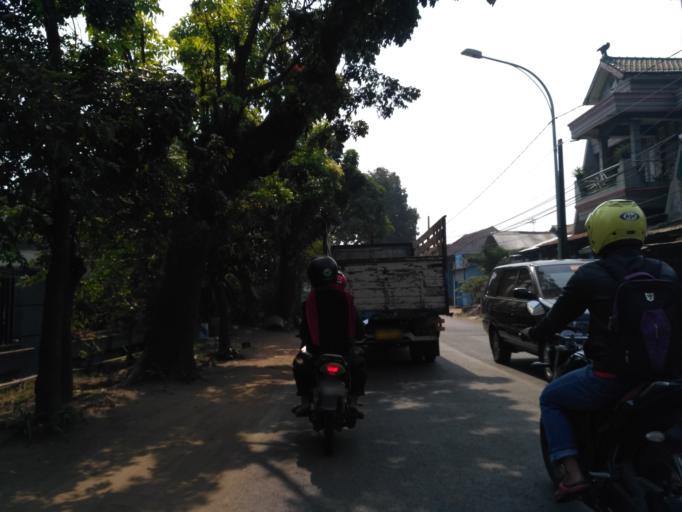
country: ID
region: East Java
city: Malang
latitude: -7.9831
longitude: 112.6609
